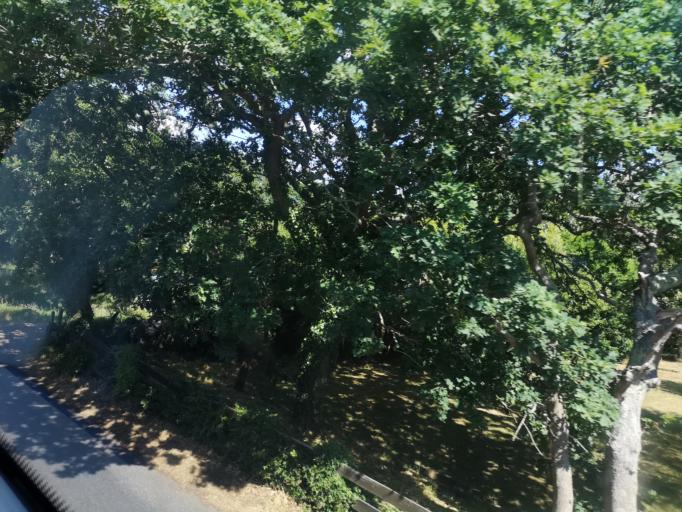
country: GB
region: England
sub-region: Isle of Wight
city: Shalfleet
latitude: 50.7030
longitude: -1.4467
